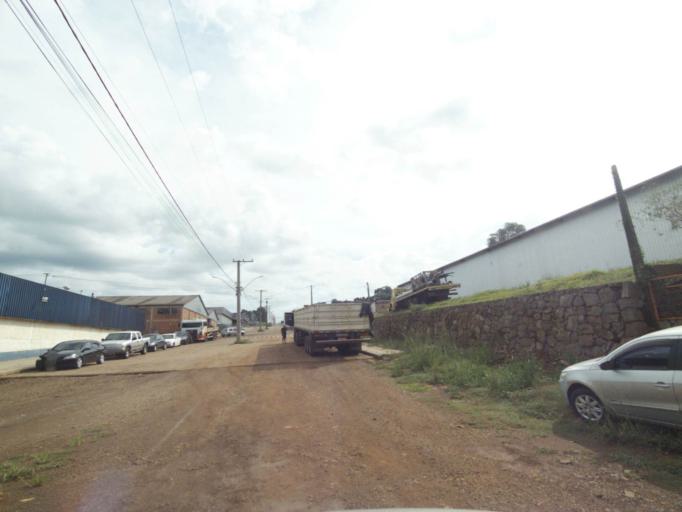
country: BR
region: Rio Grande do Sul
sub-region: Lagoa Vermelha
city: Lagoa Vermelha
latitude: -28.2312
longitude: -51.5152
